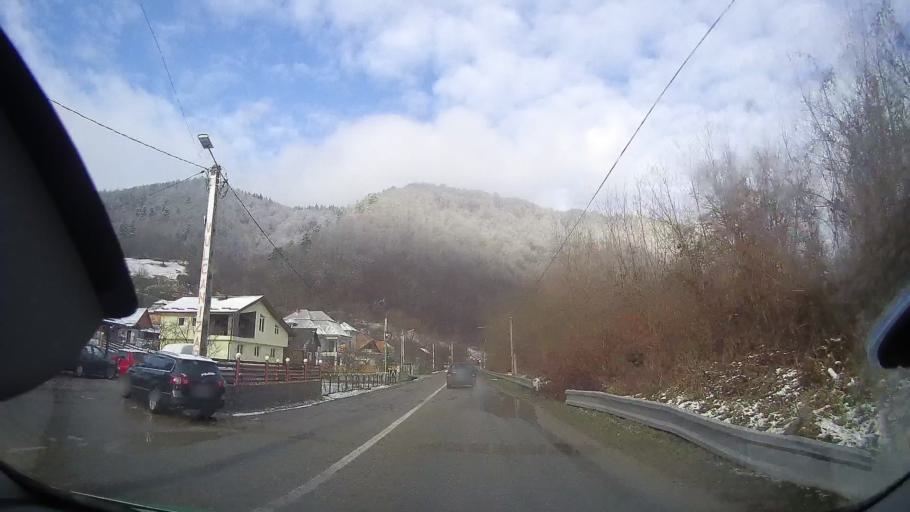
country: RO
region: Alba
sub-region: Oras Baia de Aries
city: Baia de Aries
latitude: 46.3848
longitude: 23.2812
